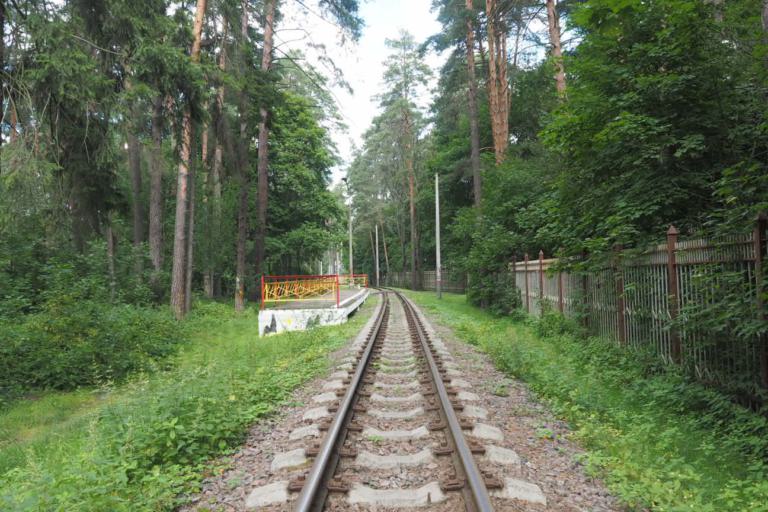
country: RU
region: Moskovskaya
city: Zhukovskiy
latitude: 55.5953
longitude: 38.1431
